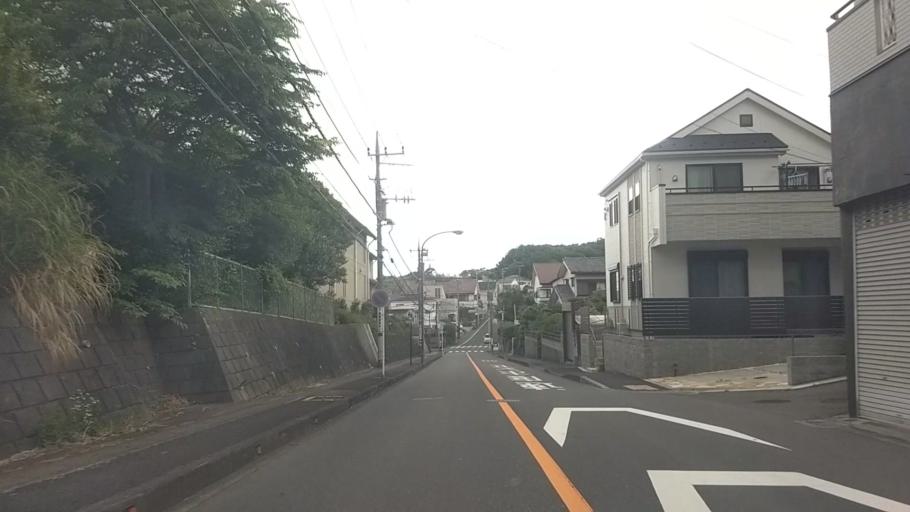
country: JP
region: Kanagawa
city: Fujisawa
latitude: 35.3574
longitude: 139.5201
